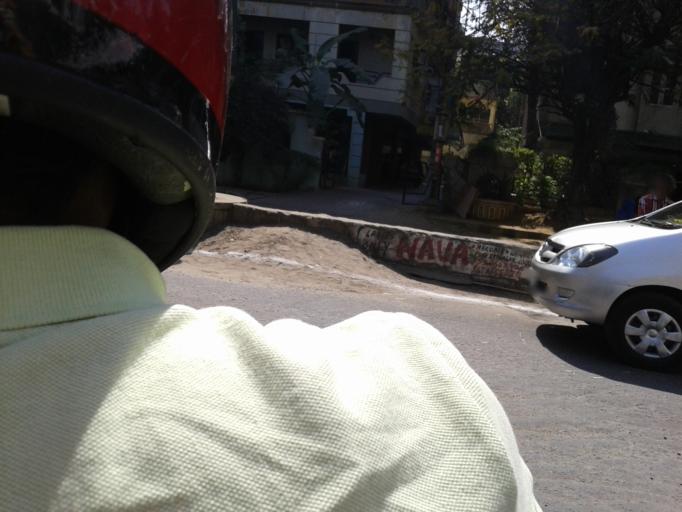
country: IN
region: Telangana
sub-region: Hyderabad
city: Hyderabad
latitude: 17.4296
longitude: 78.4390
